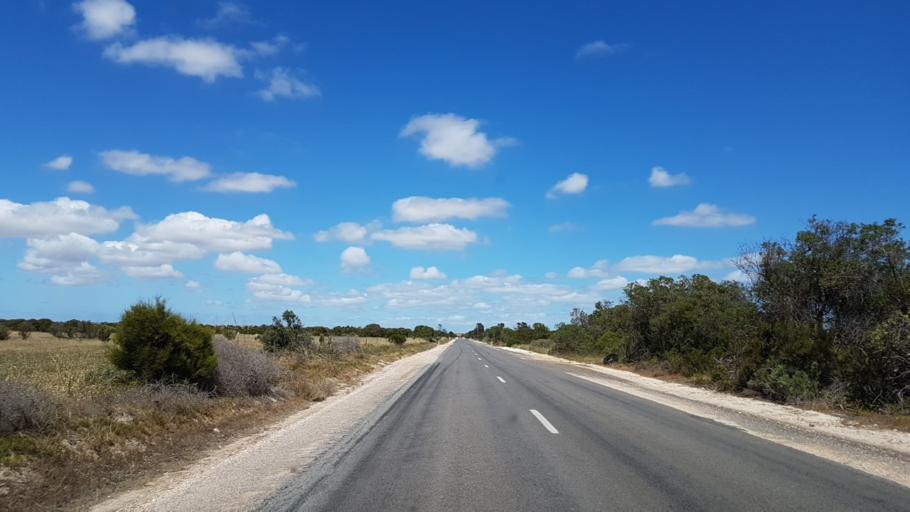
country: AU
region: South Australia
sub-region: Yorke Peninsula
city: Honiton
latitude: -34.9473
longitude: 137.4216
